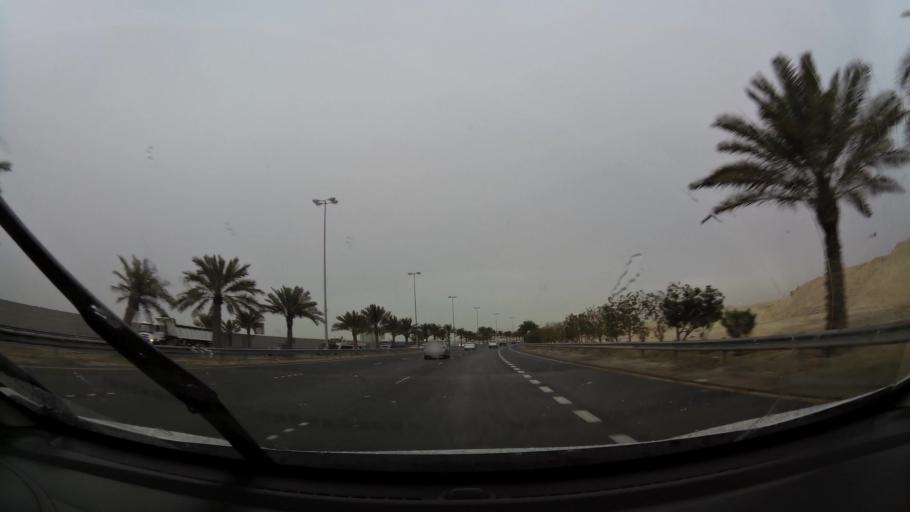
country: BH
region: Central Governorate
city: Madinat Hamad
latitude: 26.0919
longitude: 50.5146
